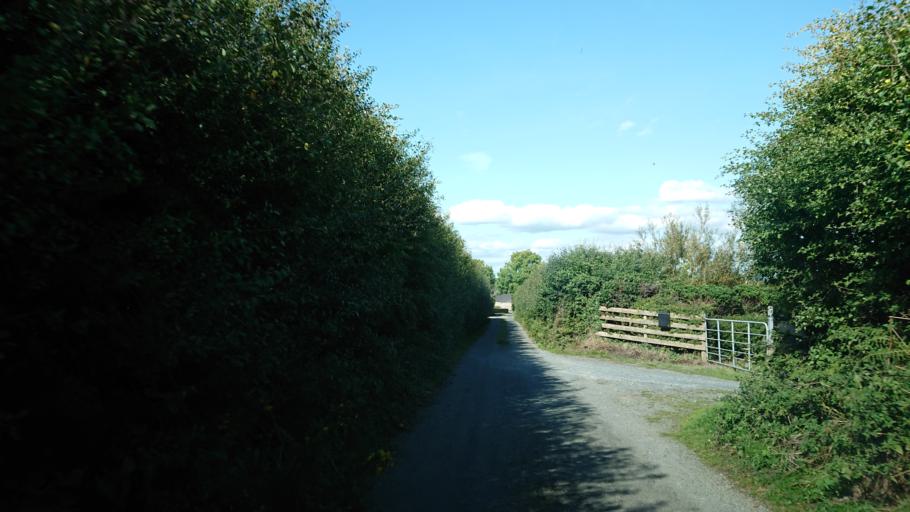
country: IE
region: Munster
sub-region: Waterford
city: Waterford
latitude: 52.2111
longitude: -7.0548
